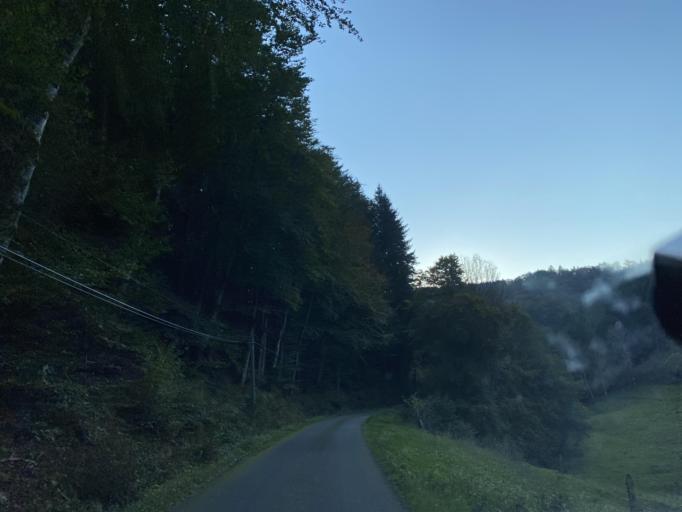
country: FR
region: Rhone-Alpes
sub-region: Departement de la Loire
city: Saint-Just-en-Chevalet
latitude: 45.9506
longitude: 3.8597
